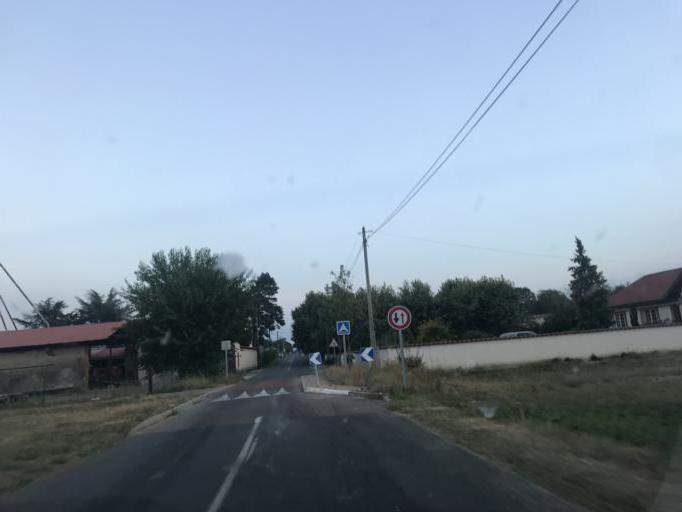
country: FR
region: Rhone-Alpes
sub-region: Departement de l'Ain
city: Chazey-sur-Ain
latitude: 45.8718
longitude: 5.2804
